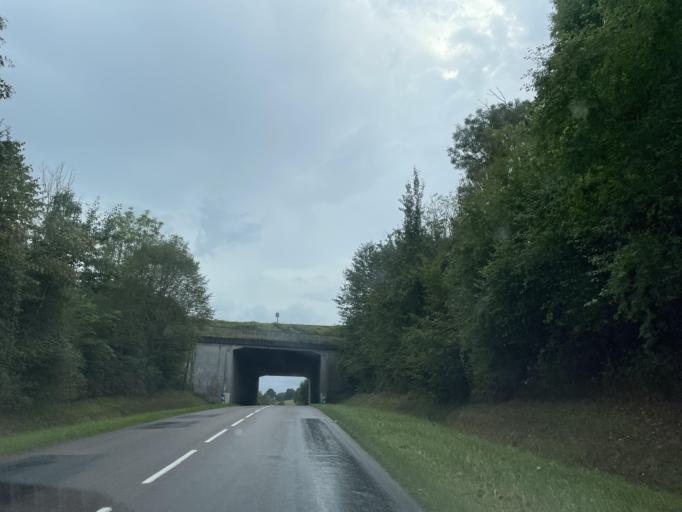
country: FR
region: Haute-Normandie
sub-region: Departement de la Seine-Maritime
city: Neufchatel-en-Bray
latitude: 49.7216
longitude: 1.4342
